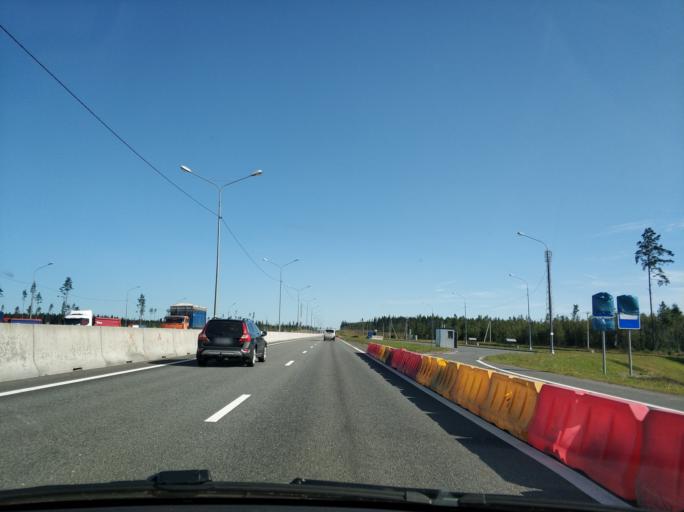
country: RU
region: Leningrad
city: Sosnovo
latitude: 60.4745
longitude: 30.1960
